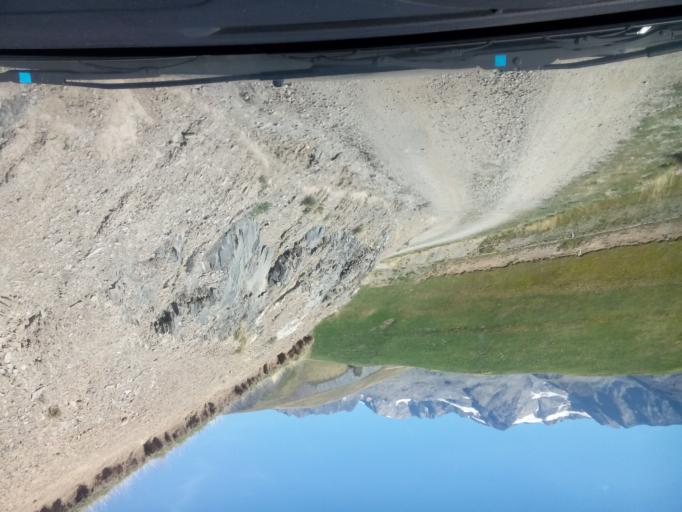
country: FR
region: Rhone-Alpes
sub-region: Departement de l'Isere
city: Mont-de-Lans
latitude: 45.0753
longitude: 6.1949
